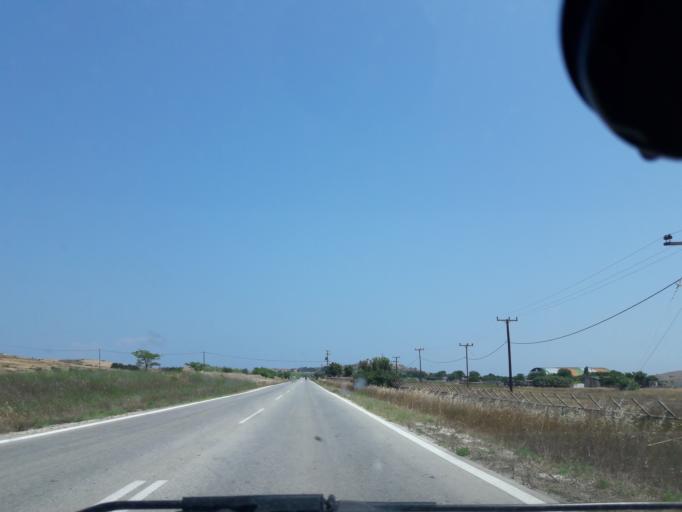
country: GR
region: North Aegean
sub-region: Nomos Lesvou
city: Myrina
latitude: 39.9273
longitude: 25.2351
